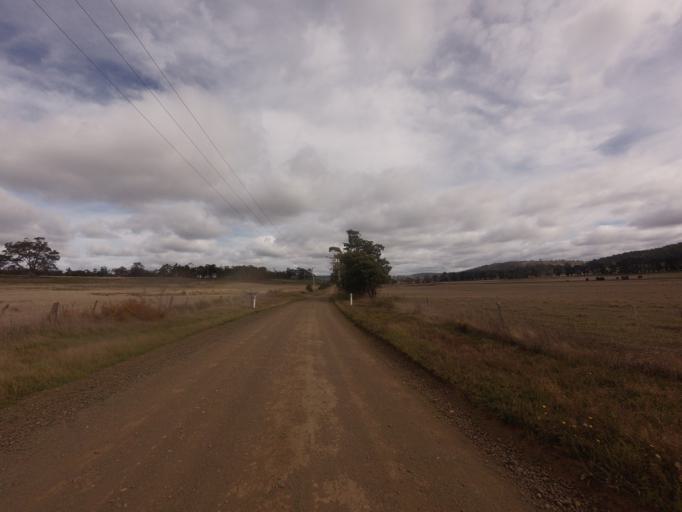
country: AU
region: Tasmania
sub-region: Brighton
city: Bridgewater
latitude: -42.3929
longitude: 147.3973
